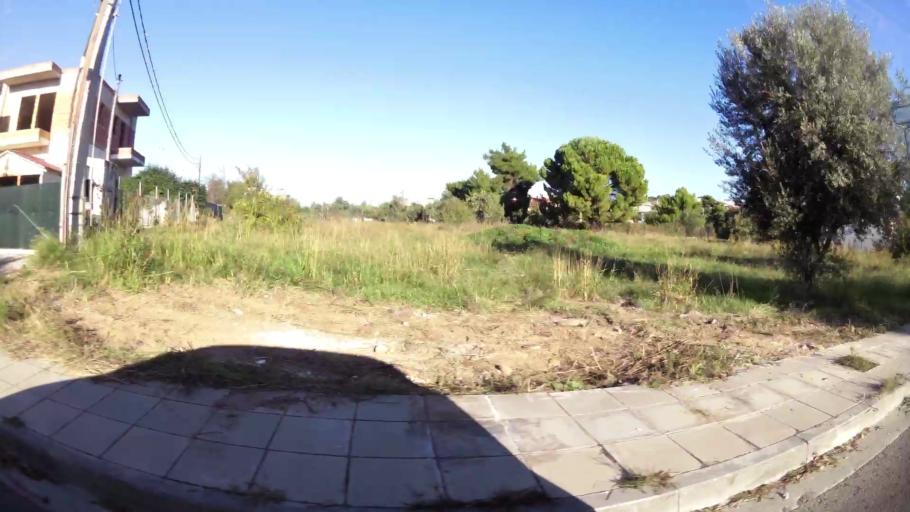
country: GR
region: Attica
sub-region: Nomarchia Anatolikis Attikis
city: Pallini
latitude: 37.9953
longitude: 23.8742
